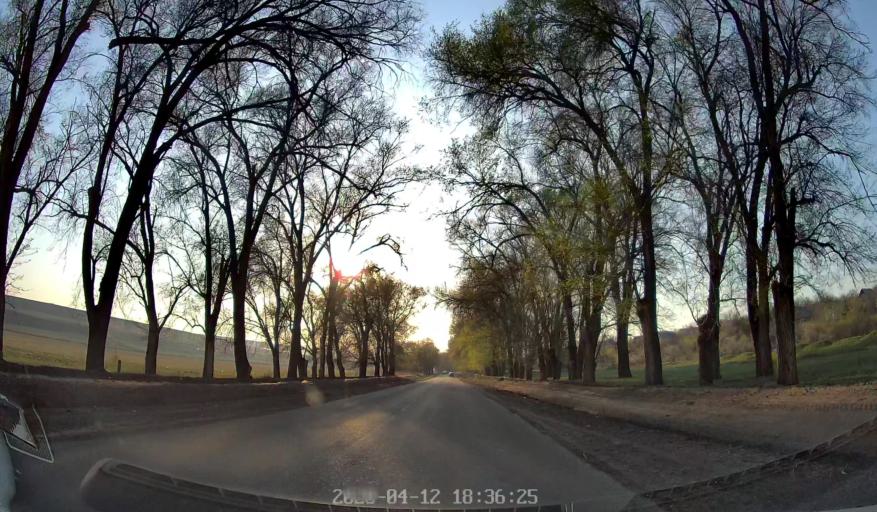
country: MD
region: Chisinau
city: Vadul lui Voda
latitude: 47.1168
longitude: 29.0306
